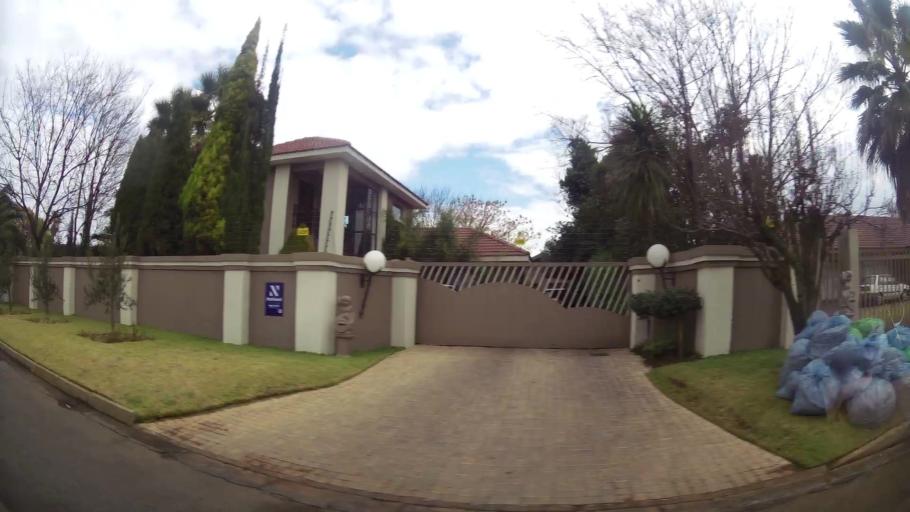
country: ZA
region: Gauteng
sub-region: Sedibeng District Municipality
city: Vereeniging
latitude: -26.6453
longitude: 27.9849
